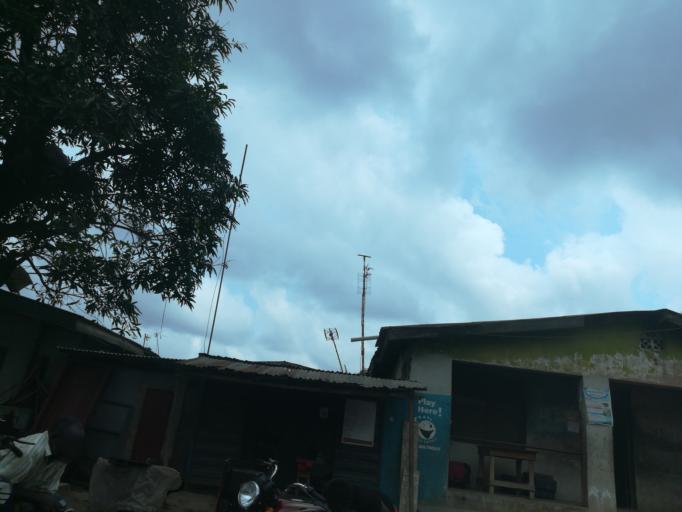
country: NG
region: Lagos
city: Oshodi
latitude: 6.5567
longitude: 3.3393
